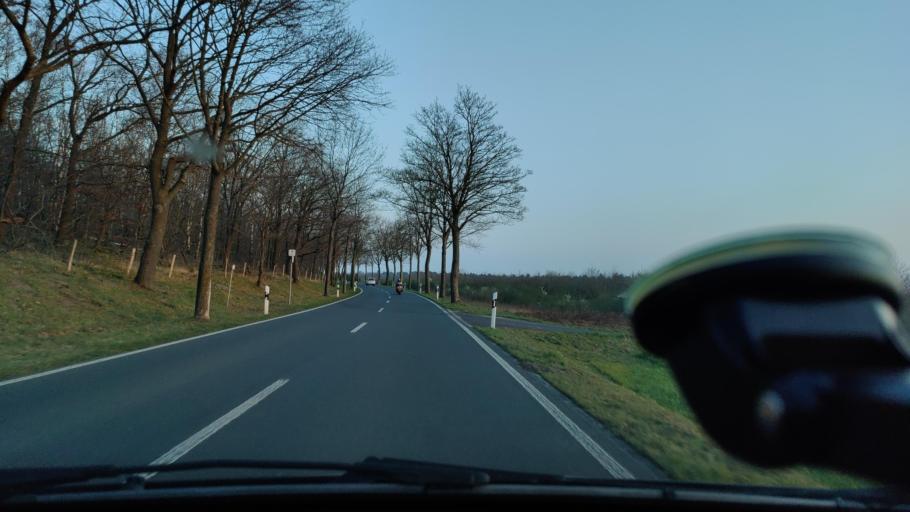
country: NL
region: Limburg
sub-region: Gemeente Bergen
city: Wellerlooi
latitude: 51.6021
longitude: 6.1132
